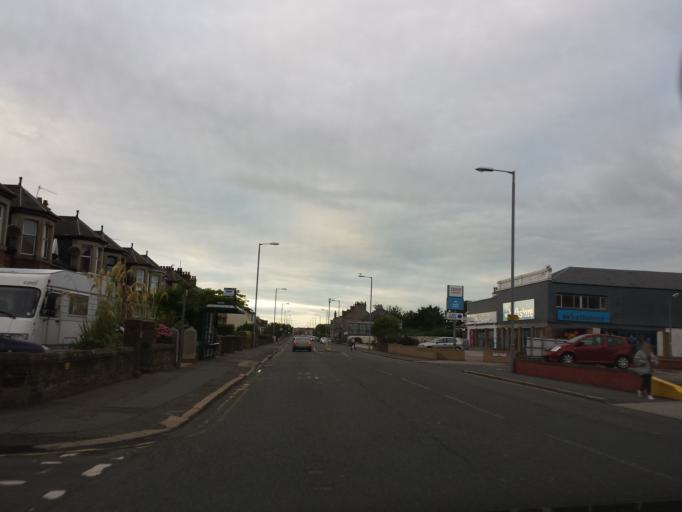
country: GB
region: Scotland
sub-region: South Ayrshire
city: Prestwick
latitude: 55.4772
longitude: -4.6224
